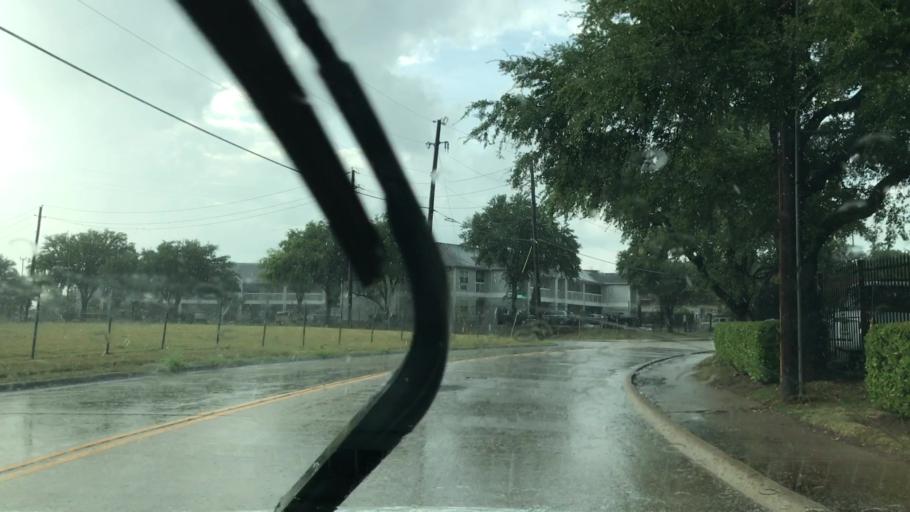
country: US
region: Texas
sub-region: Dallas County
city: Richardson
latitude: 32.9004
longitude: -96.7137
